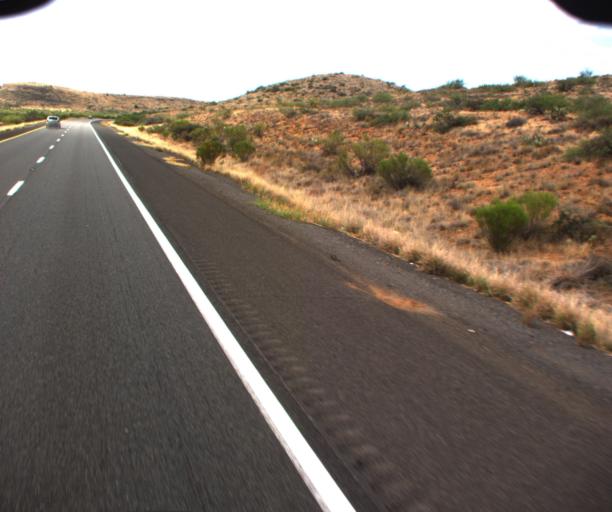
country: US
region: Arizona
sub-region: Yavapai County
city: Cordes Lakes
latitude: 34.2465
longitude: -112.1138
